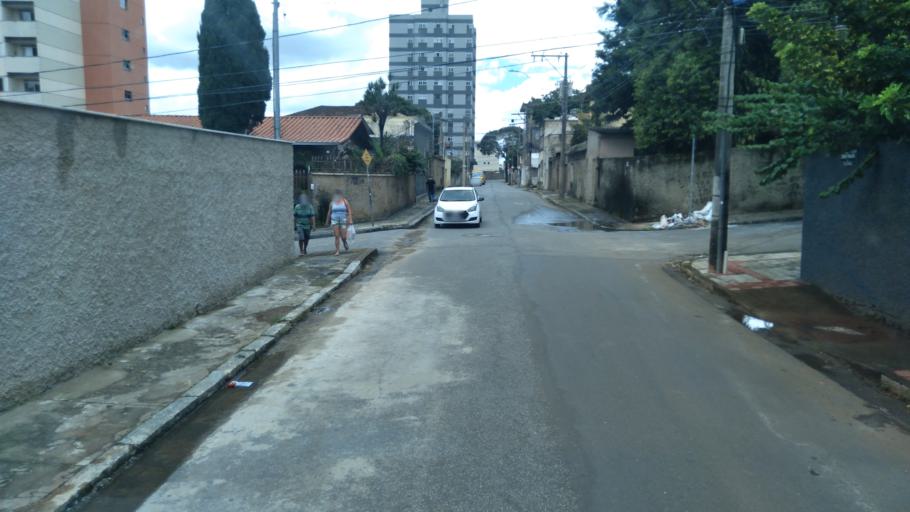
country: BR
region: Minas Gerais
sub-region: Belo Horizonte
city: Belo Horizonte
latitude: -19.9185
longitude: -43.9082
